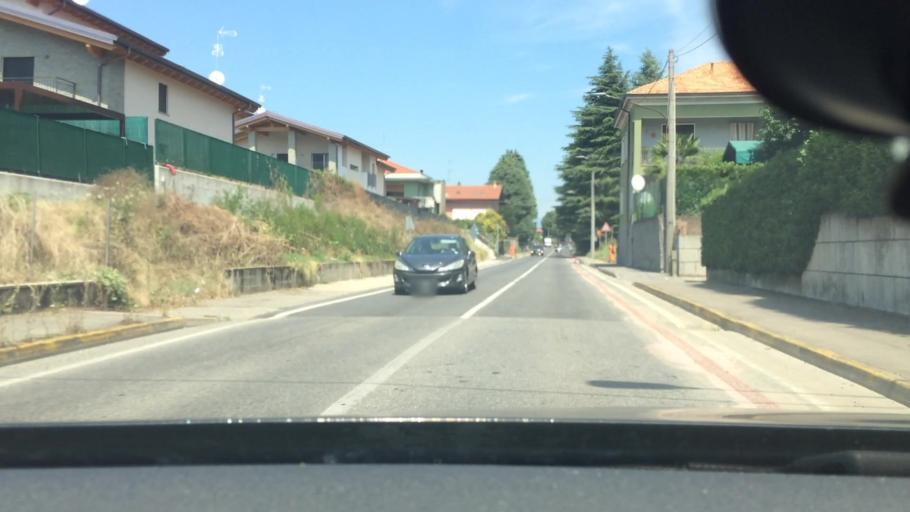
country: IT
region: Lombardy
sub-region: Provincia di Como
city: Turate
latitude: 45.6533
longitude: 8.9976
